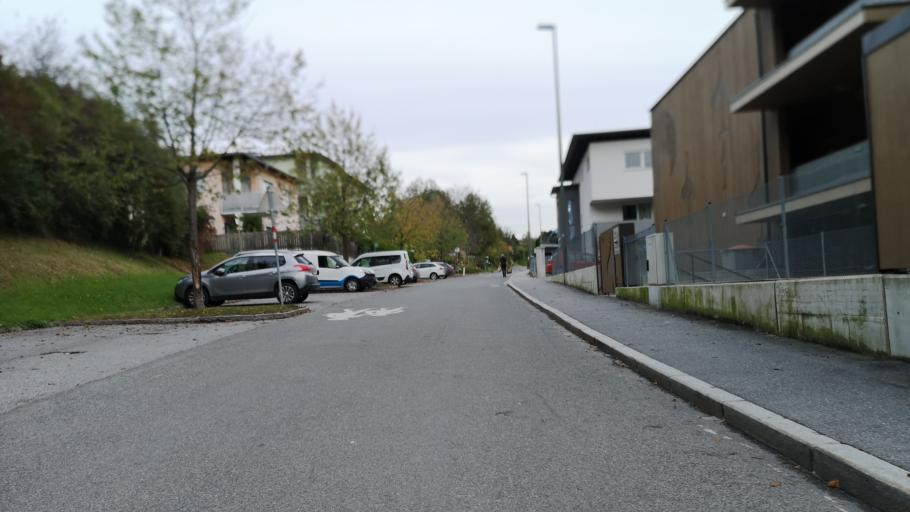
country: AT
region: Tyrol
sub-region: Politischer Bezirk Innsbruck Land
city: Vols
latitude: 47.2672
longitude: 11.3571
